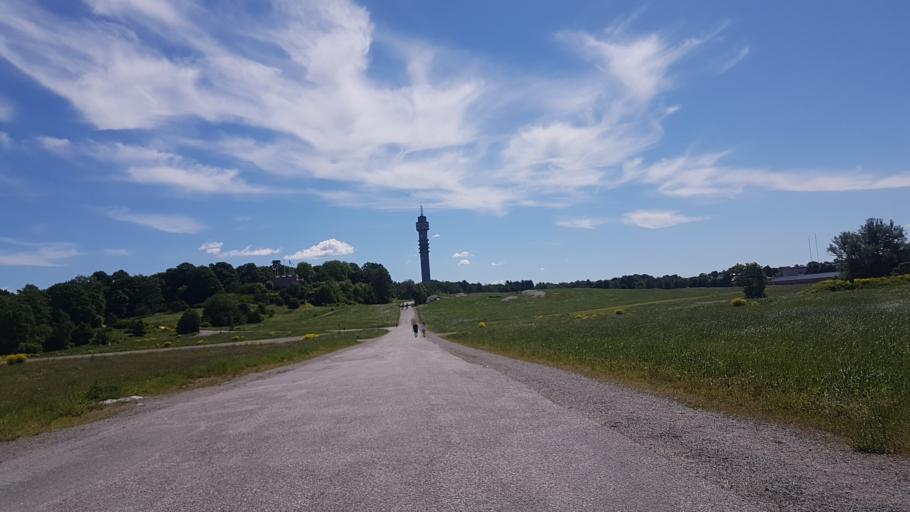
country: SE
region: Stockholm
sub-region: Stockholms Kommun
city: OEstermalm
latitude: 59.3388
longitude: 18.1091
